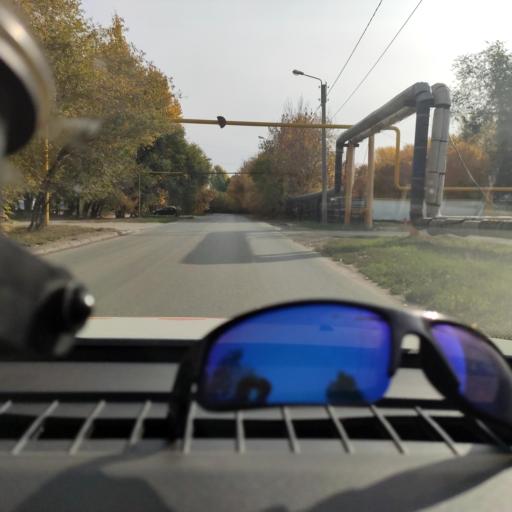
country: RU
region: Samara
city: Samara
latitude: 53.1194
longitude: 50.0895
